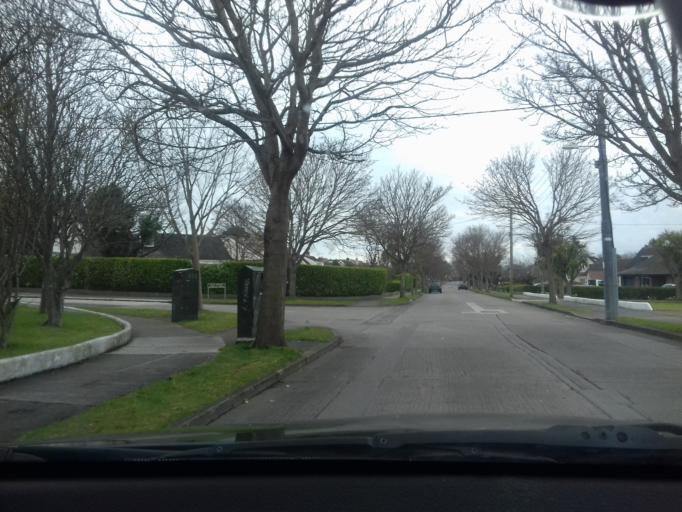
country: IE
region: Leinster
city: Sutton
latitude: 53.3898
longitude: -6.0976
